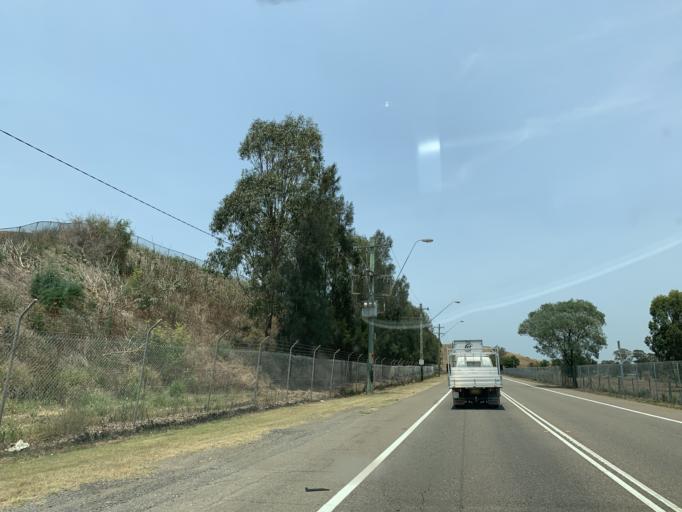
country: AU
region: New South Wales
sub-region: Blacktown
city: Doonside
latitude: -33.8052
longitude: 150.8643
